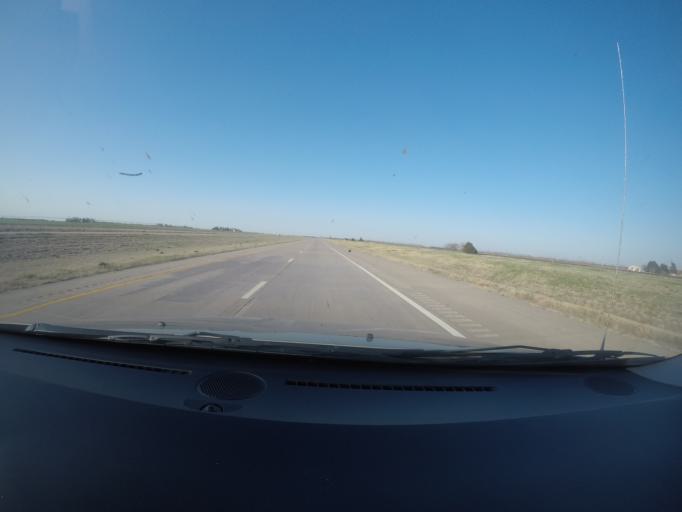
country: US
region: Kansas
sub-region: McPherson County
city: Inman
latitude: 38.2981
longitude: -97.7253
